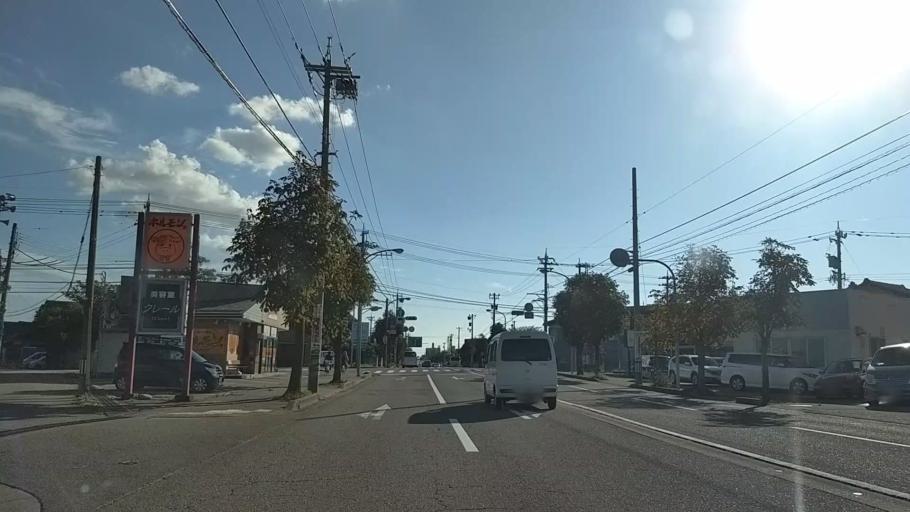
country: JP
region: Ishikawa
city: Kanazawa-shi
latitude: 36.5775
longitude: 136.6350
